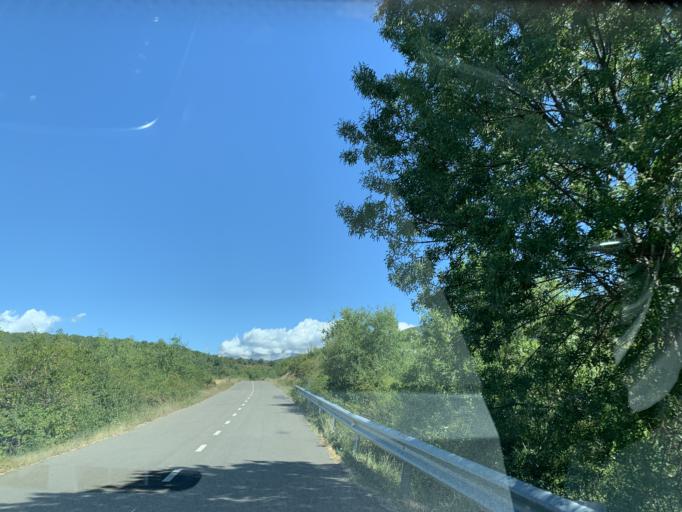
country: ES
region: Aragon
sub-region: Provincia de Huesca
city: Sabinanigo
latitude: 42.5364
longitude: -0.3209
